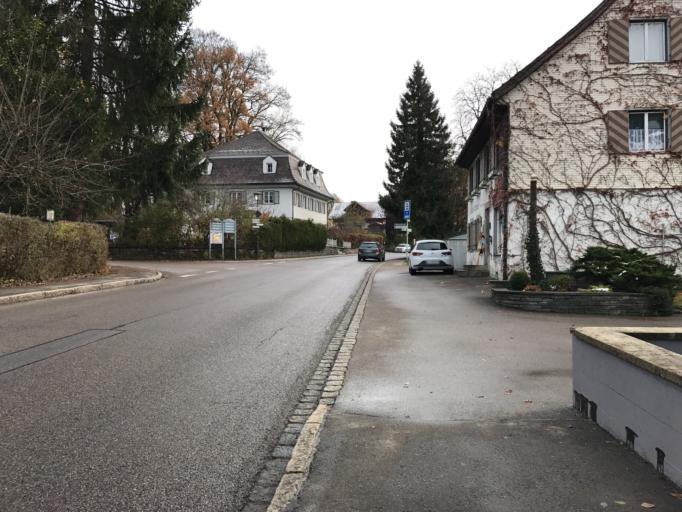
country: DE
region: Bavaria
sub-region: Swabia
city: Weiler-Simmerberg
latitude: 47.5822
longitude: 9.9117
